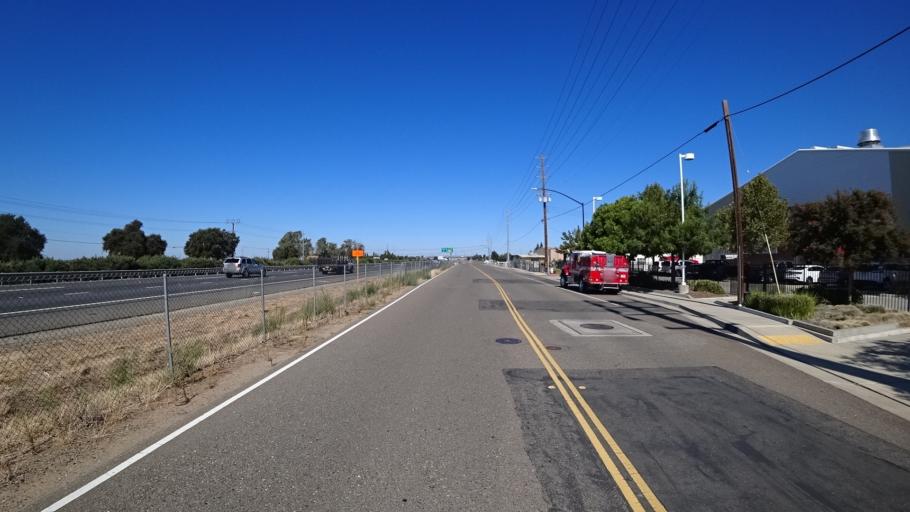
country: US
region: California
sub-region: Sacramento County
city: Elk Grove
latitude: 38.3715
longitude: -121.3567
